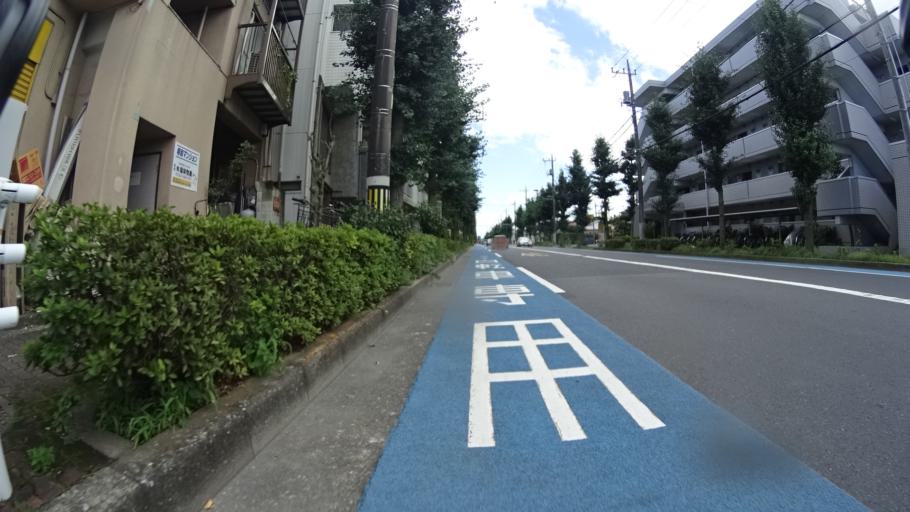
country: JP
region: Tokyo
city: Fussa
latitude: 35.7606
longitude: 139.3107
